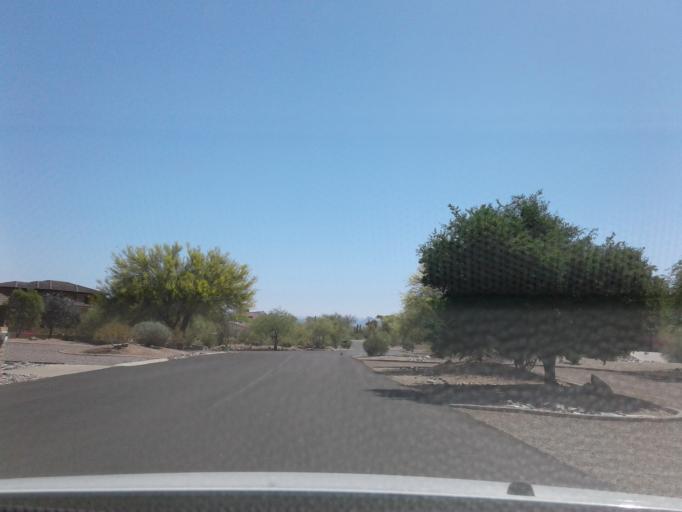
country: US
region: Arizona
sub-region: Maricopa County
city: Paradise Valley
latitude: 33.5610
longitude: -111.9827
